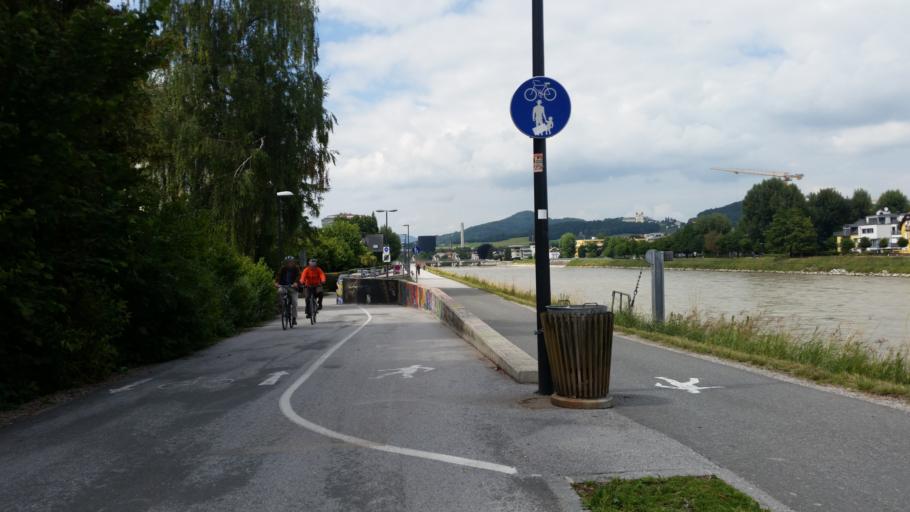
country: AT
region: Salzburg
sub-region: Politischer Bezirk Salzburg-Umgebung
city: Bergheim
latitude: 47.8159
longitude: 13.0356
